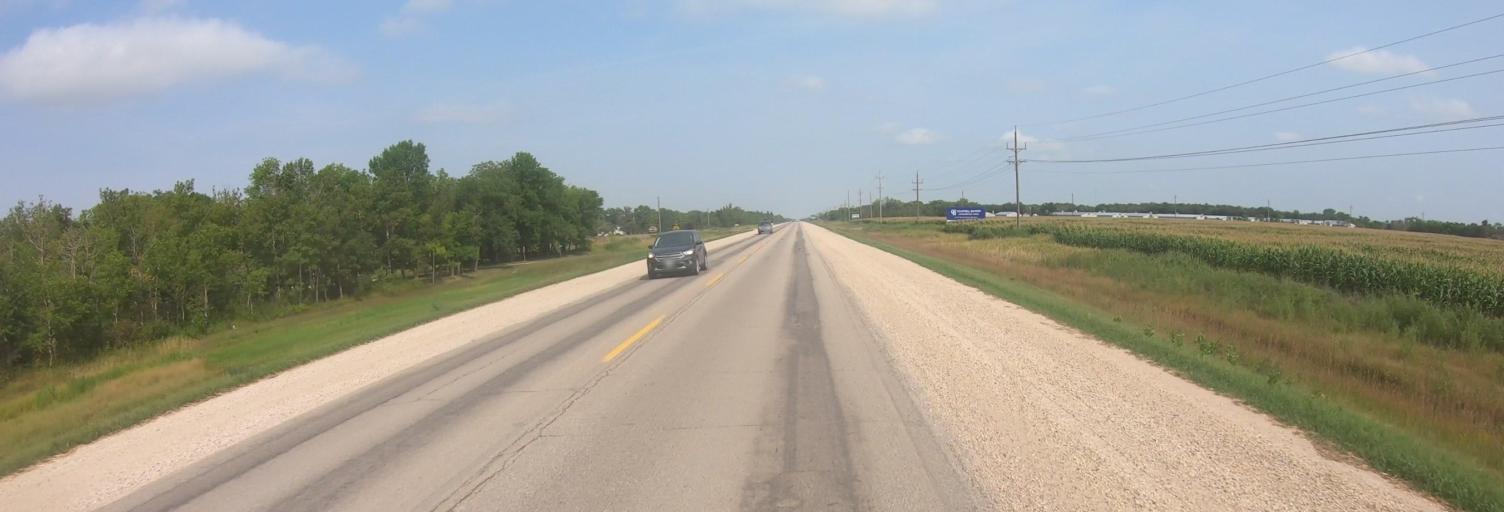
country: CA
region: Manitoba
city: Steinbach
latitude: 49.4840
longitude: -96.6911
